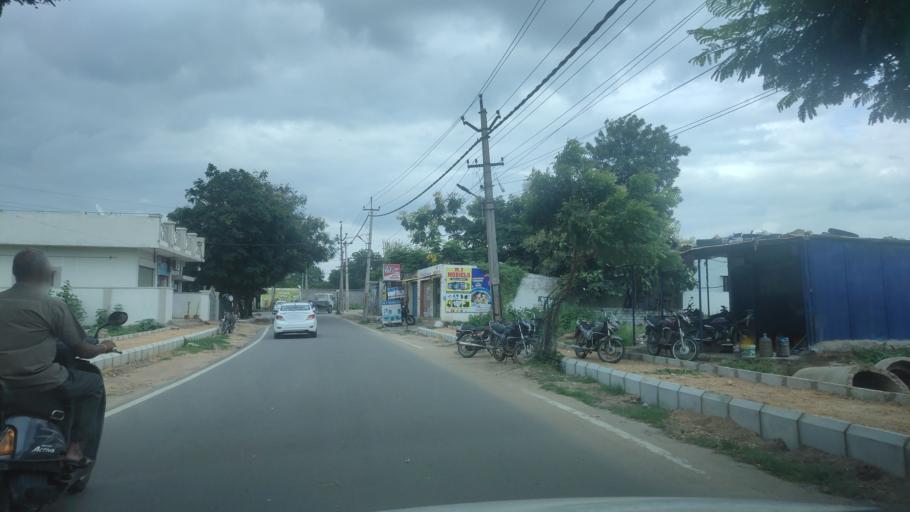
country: IN
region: Telangana
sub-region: Medak
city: Serilingampalle
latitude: 17.5011
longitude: 78.3497
